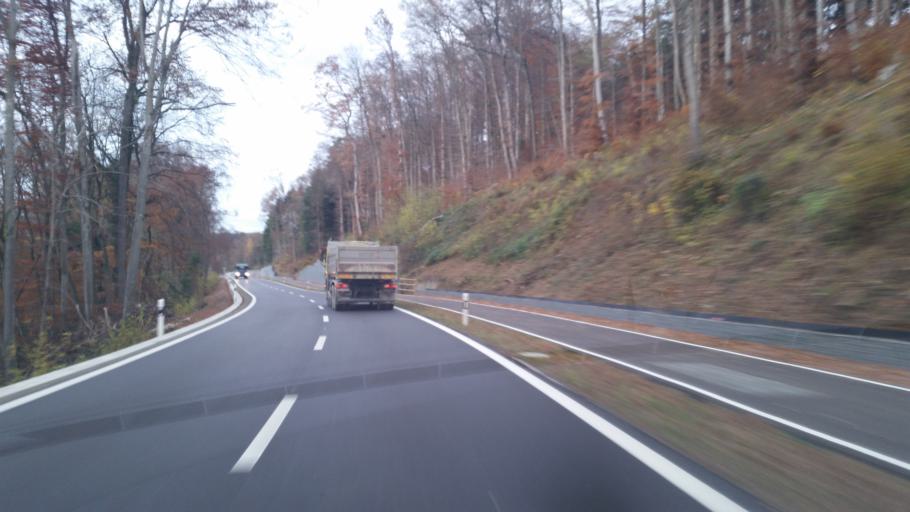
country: CH
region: Aargau
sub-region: Bezirk Baden
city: Kunten
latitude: 47.3779
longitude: 8.3324
